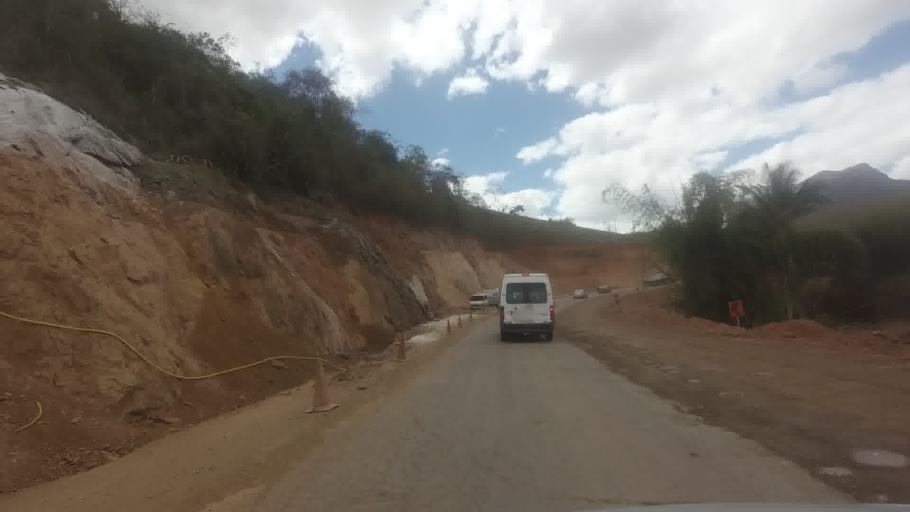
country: BR
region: Rio de Janeiro
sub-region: Santo Antonio De Padua
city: Santo Antonio de Padua
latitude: -21.5146
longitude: -42.0957
